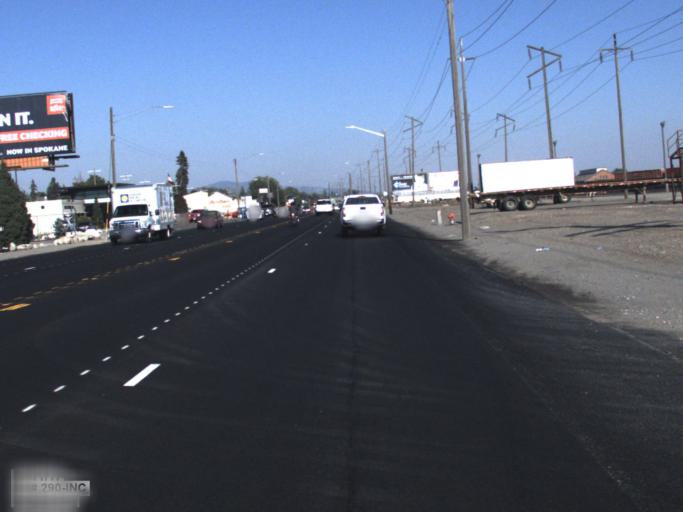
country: US
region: Washington
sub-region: Spokane County
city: Millwood
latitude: 47.6732
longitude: -117.3383
